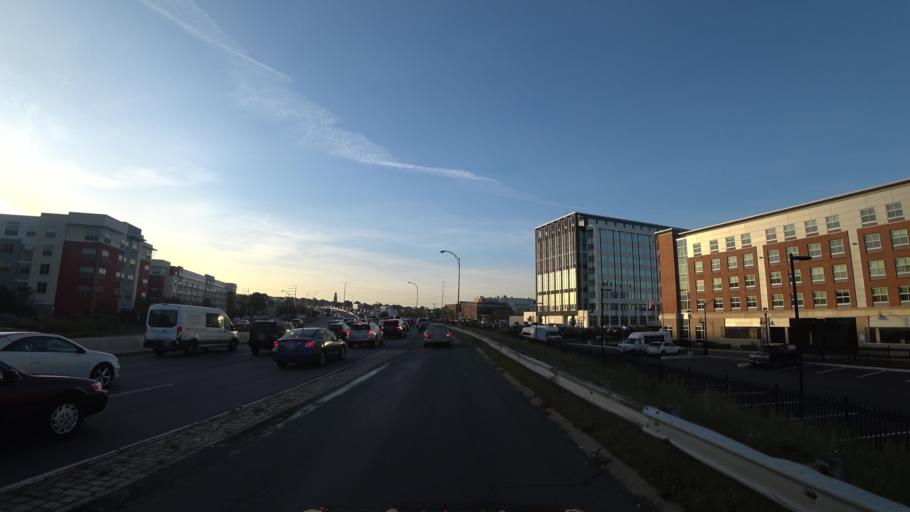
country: US
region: Massachusetts
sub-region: Suffolk County
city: Chelsea
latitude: 42.3989
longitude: -71.0385
